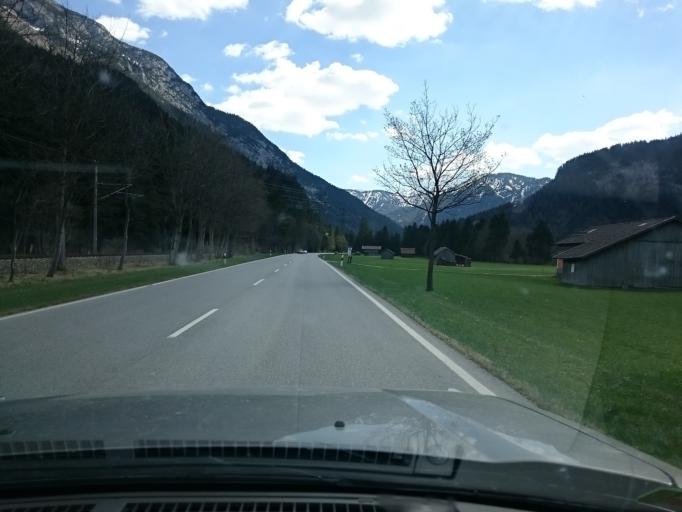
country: AT
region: Tyrol
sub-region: Politischer Bezirk Innsbruck Land
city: Scharnitz
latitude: 47.4092
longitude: 11.2596
